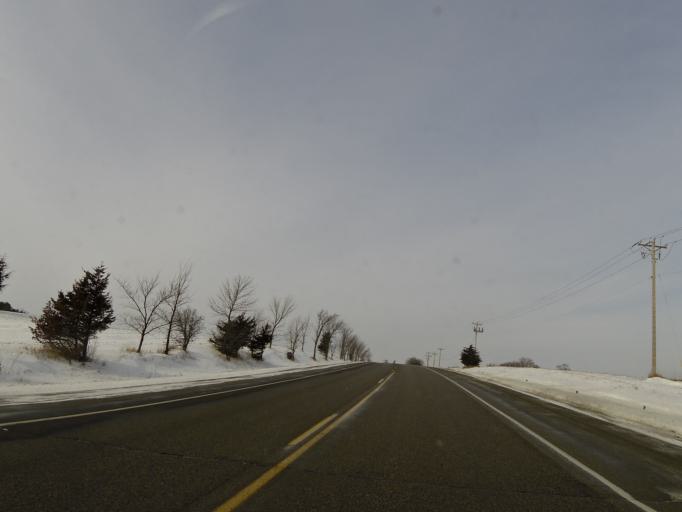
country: US
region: Minnesota
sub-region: Hennepin County
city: Saint Bonifacius
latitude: 44.8956
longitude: -93.7143
